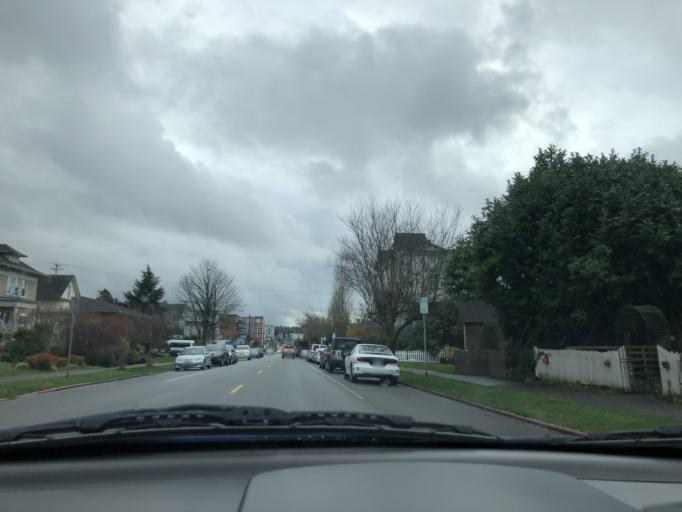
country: US
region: Washington
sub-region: Snohomish County
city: Everett
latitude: 47.9846
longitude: -122.2113
